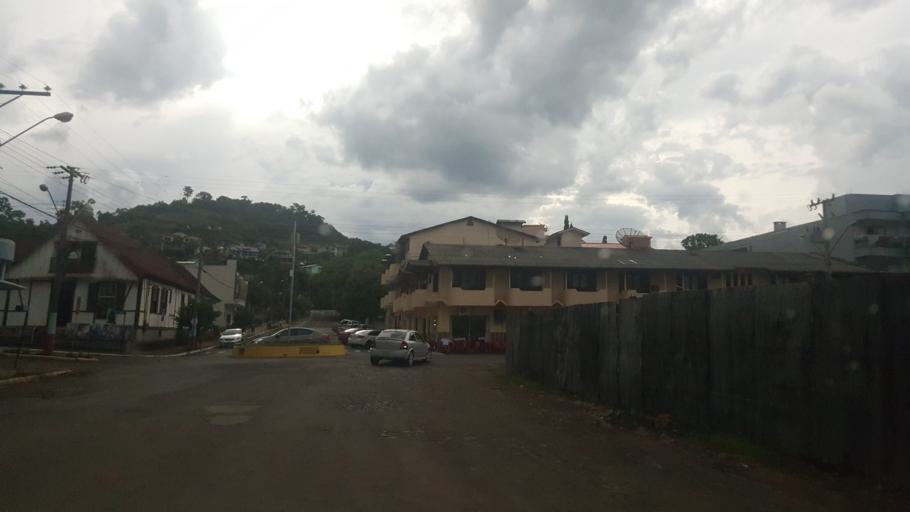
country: BR
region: Rio Grande do Sul
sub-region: Frederico Westphalen
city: Frederico Westphalen
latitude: -27.1059
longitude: -53.3985
